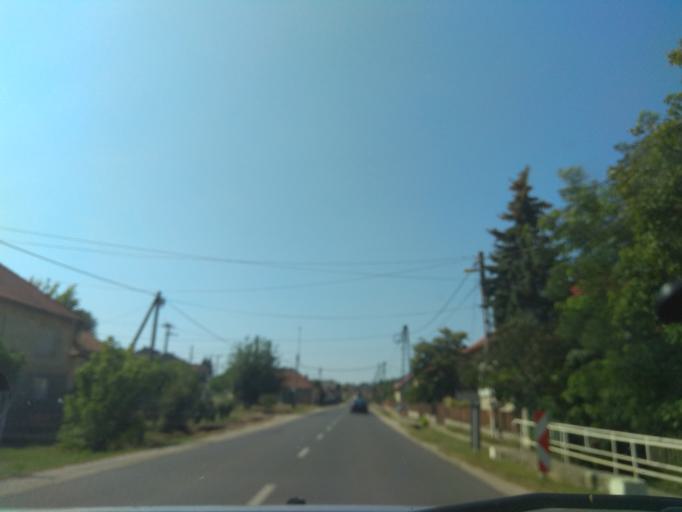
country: HU
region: Borsod-Abauj-Zemplen
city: Harsany
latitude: 47.9730
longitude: 20.7417
